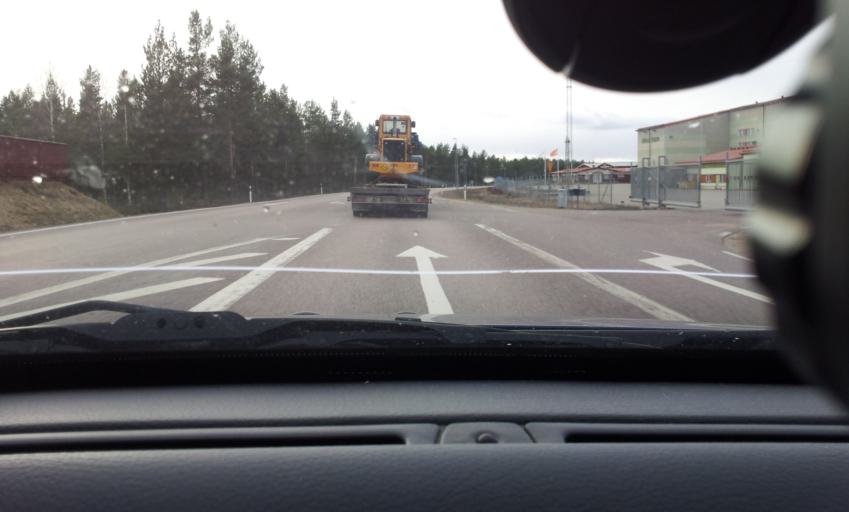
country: SE
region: Gaevleborg
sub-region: Ljusdals Kommun
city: Farila
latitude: 61.8032
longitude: 15.7866
